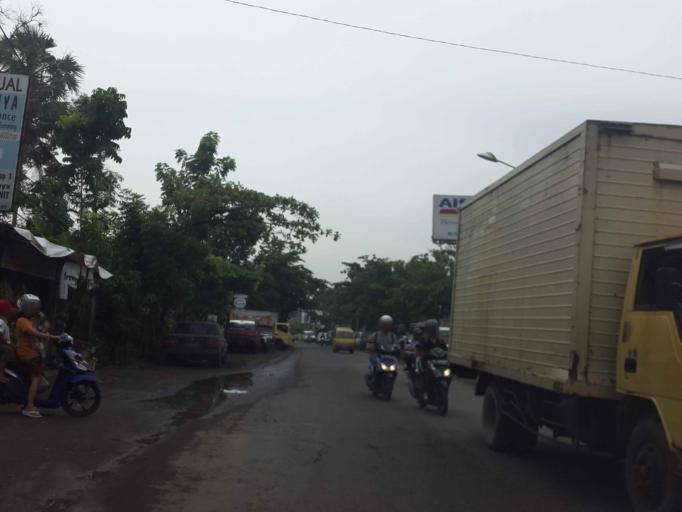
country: ID
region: Central Java
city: Semarang
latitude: -6.9920
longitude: 110.4731
